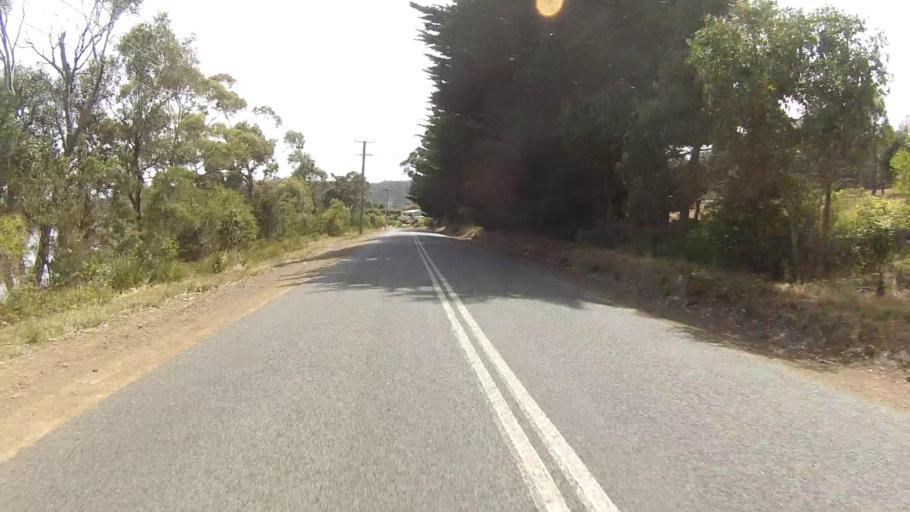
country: AU
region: Tasmania
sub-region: Huon Valley
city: Cygnet
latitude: -43.1940
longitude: 147.1020
